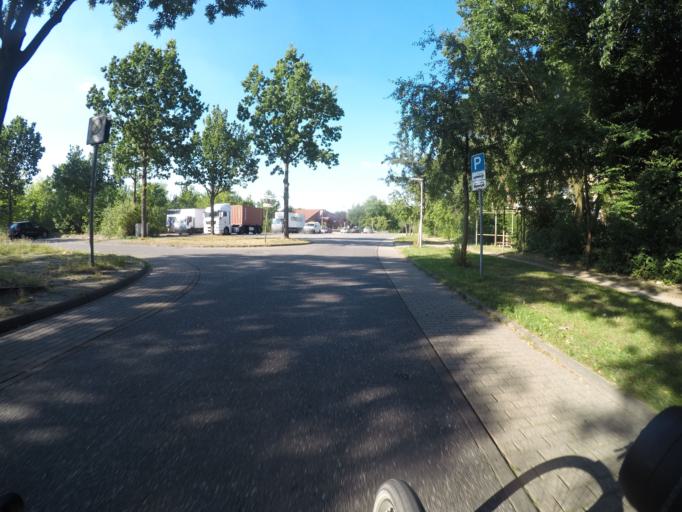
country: DE
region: Schleswig-Holstein
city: Oststeinbek
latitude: 53.5325
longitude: 10.1504
